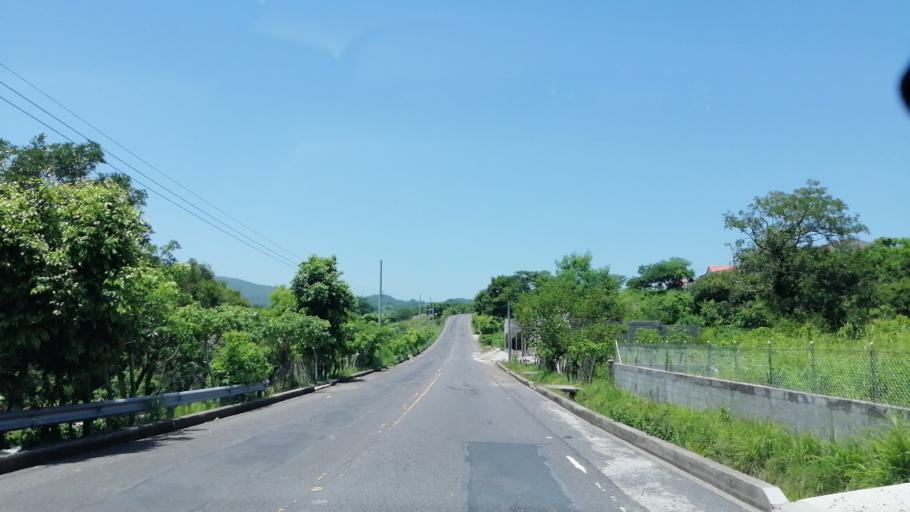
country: SV
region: Chalatenango
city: Chalatenango
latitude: 14.0302
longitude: -88.9464
